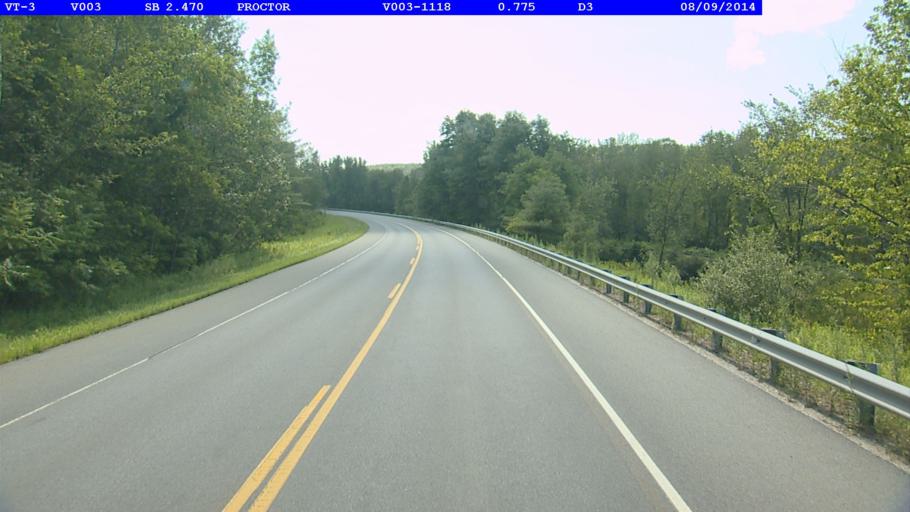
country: US
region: Vermont
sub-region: Rutland County
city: West Rutland
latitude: 43.6351
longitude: -73.0347
